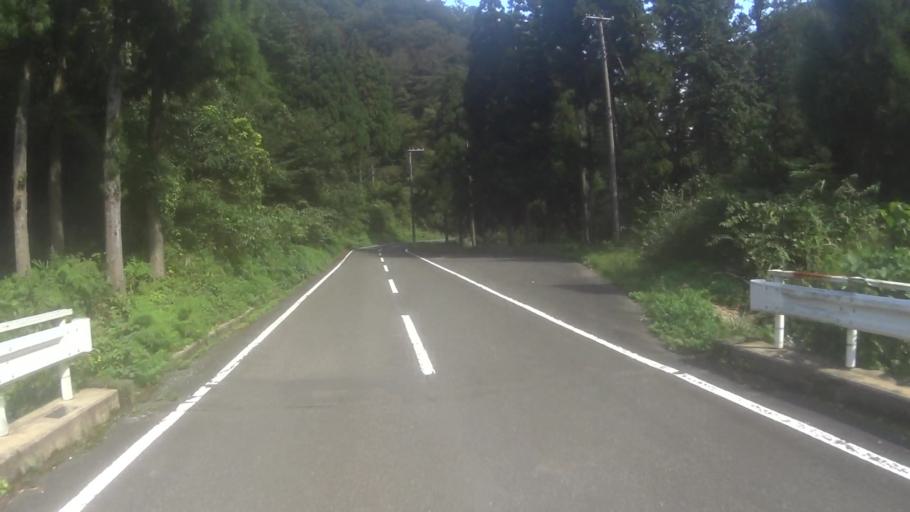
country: JP
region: Kyoto
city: Miyazu
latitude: 35.6777
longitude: 135.1546
